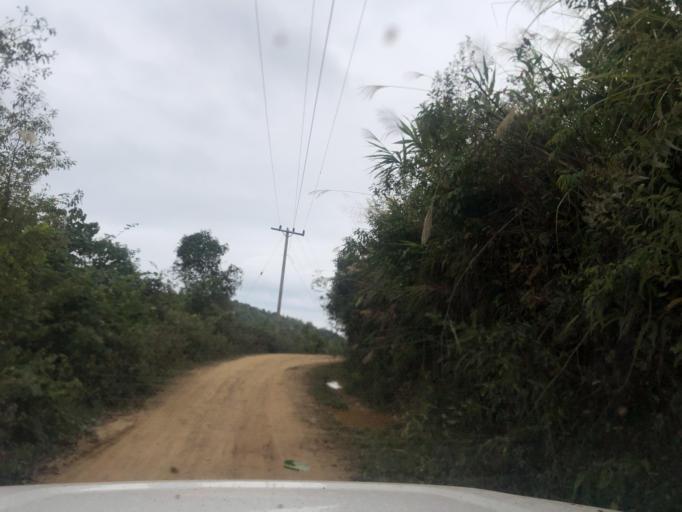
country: LA
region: Phongsali
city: Khoa
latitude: 21.2577
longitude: 102.5897
